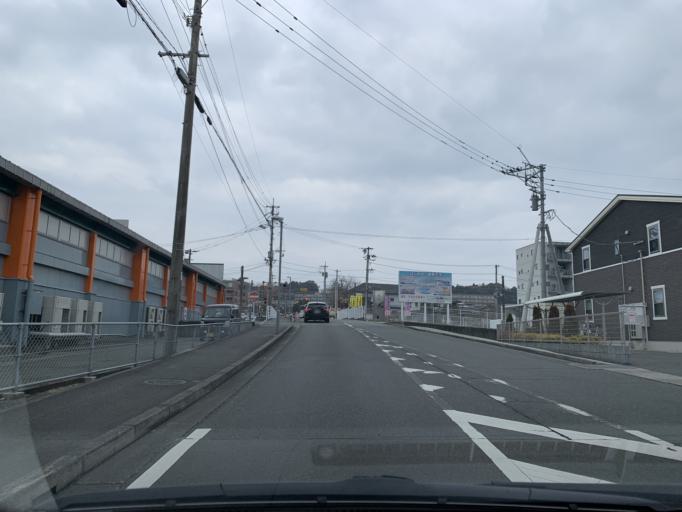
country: JP
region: Kumamoto
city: Ozu
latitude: 32.8763
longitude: 130.8579
